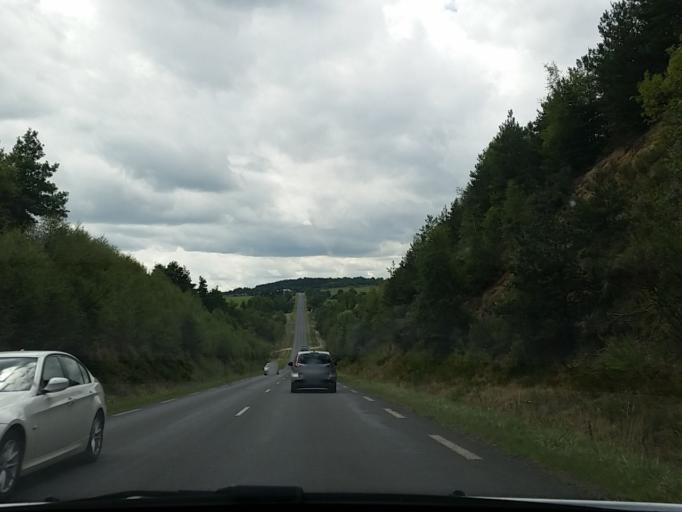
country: FR
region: Auvergne
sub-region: Departement du Cantal
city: Saint-Flour
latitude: 45.0152
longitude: 3.0531
